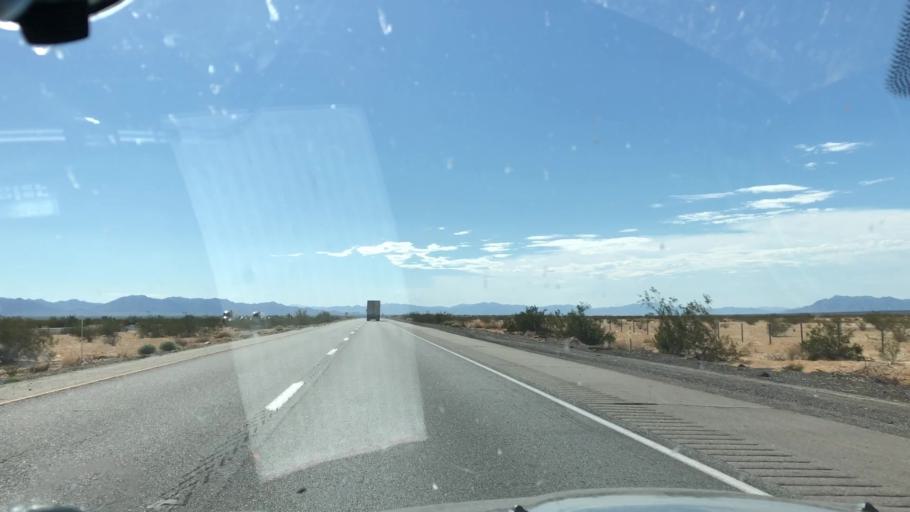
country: US
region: California
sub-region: Riverside County
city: Mesa Verde
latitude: 33.6286
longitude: -115.0652
